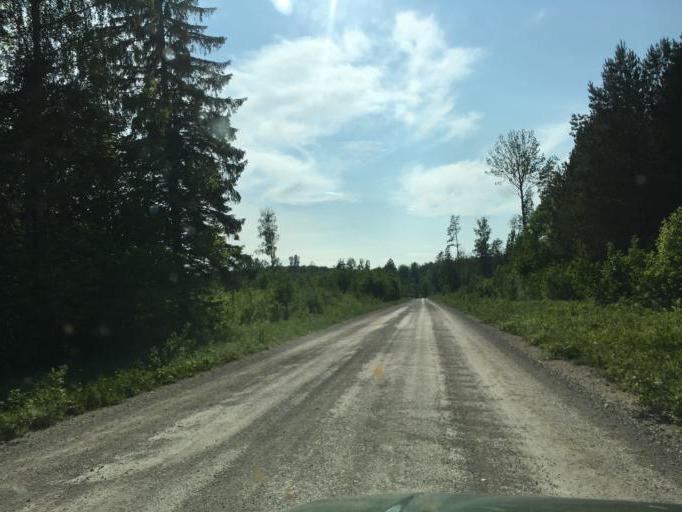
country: LV
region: Dundaga
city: Dundaga
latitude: 57.6122
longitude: 22.4900
